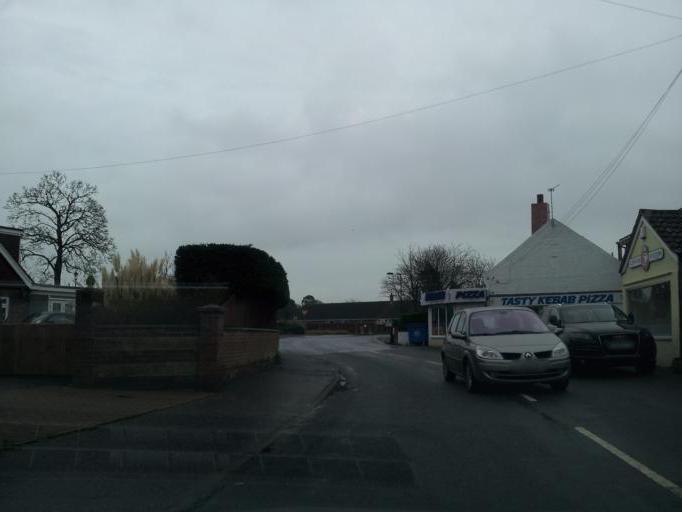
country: GB
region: England
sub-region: Norfolk
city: Hemsby
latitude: 52.6971
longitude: 1.6907
